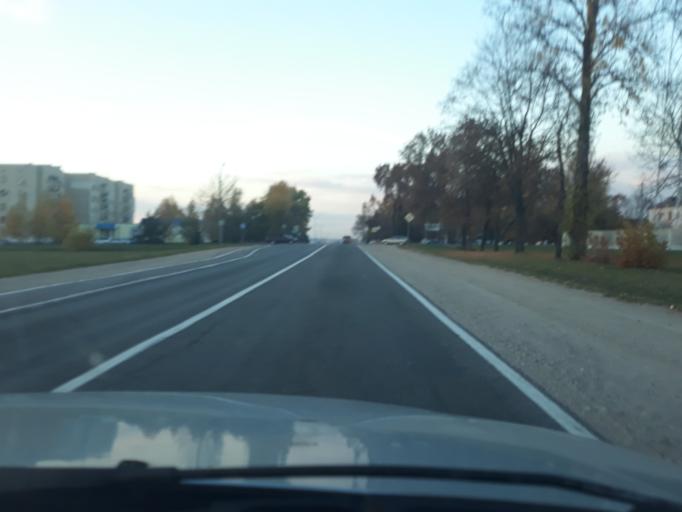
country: BY
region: Grodnenskaya
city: Vawkavysk
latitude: 53.1469
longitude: 24.4626
